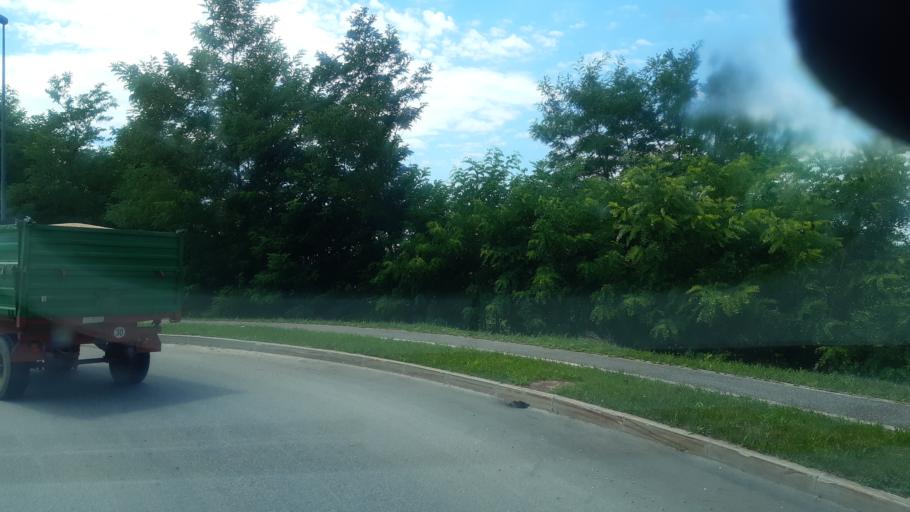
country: SI
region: Beltinci
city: Gancani
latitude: 46.6400
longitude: 16.2616
